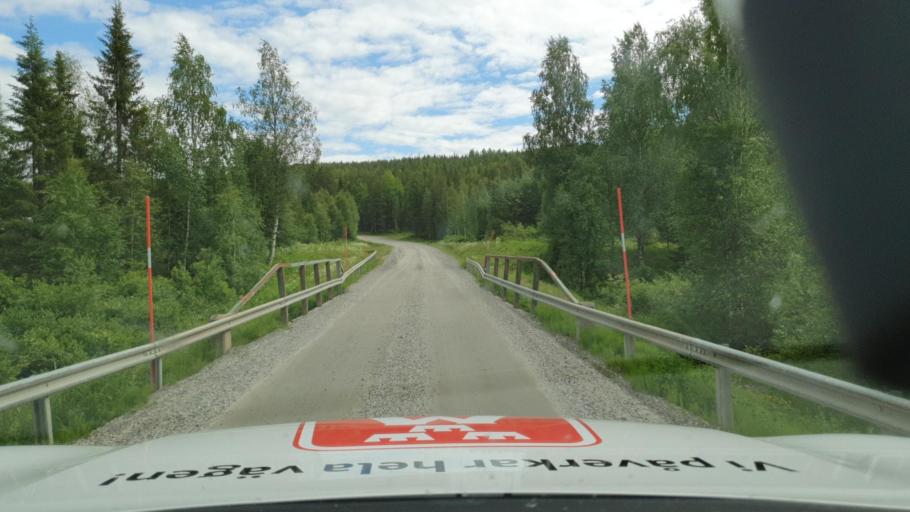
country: SE
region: Vaesterbotten
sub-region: Norsjo Kommun
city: Norsjoe
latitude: 64.8333
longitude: 19.5390
